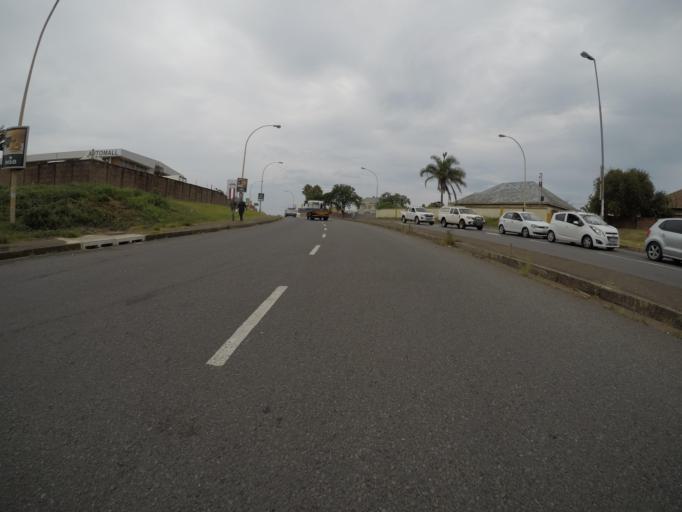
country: ZA
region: Eastern Cape
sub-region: Buffalo City Metropolitan Municipality
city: East London
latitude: -32.9843
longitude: 27.8976
